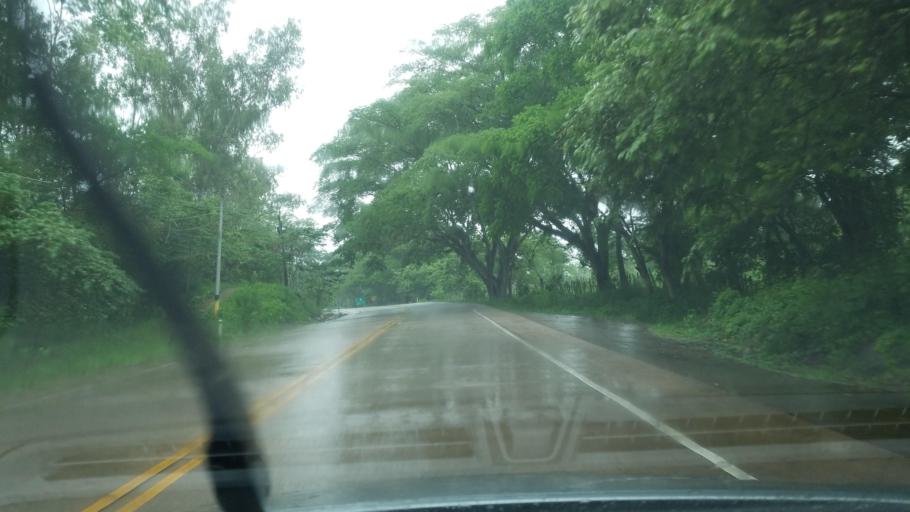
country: HN
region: Copan
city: Copan
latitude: 14.8435
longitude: -89.1414
